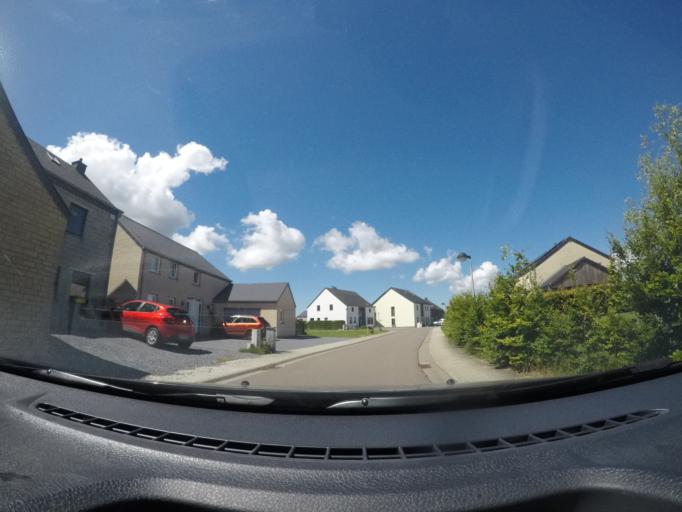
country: BE
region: Wallonia
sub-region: Province du Luxembourg
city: Tintigny
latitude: 49.6808
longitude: 5.5213
